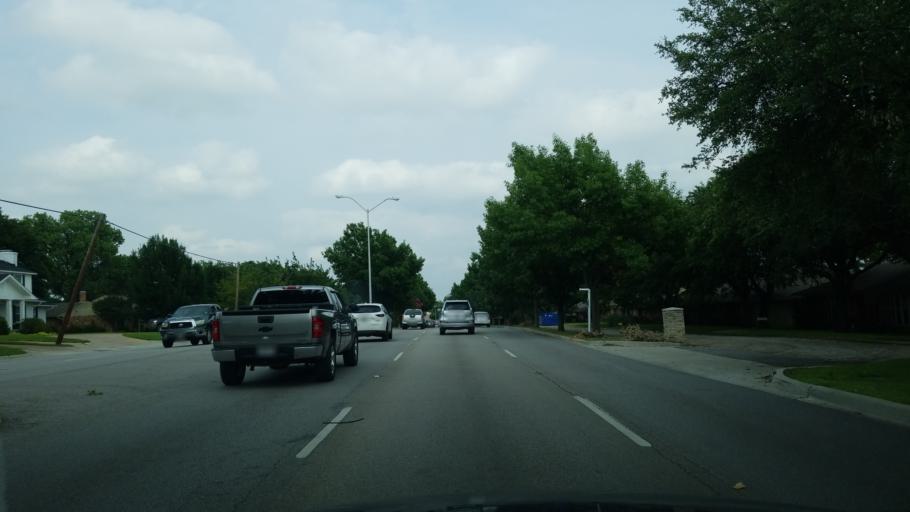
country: US
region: Texas
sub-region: Dallas County
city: Farmers Branch
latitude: 32.8951
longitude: -96.8546
